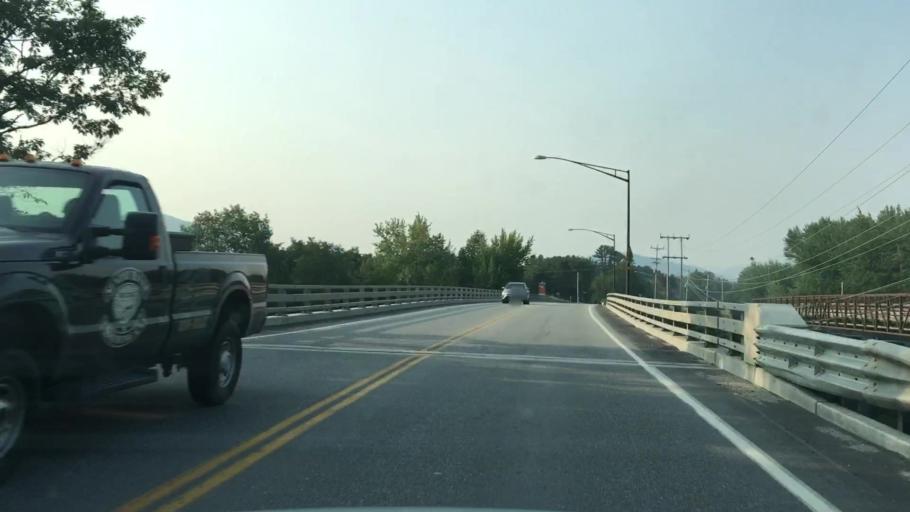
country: US
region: Maine
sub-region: Oxford County
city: Bethel
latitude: 44.4160
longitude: -70.7970
